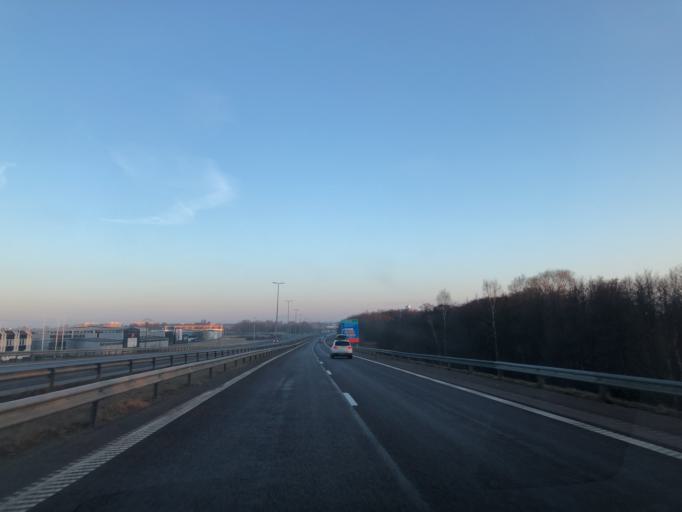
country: SE
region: Halland
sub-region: Halmstads Kommun
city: Fyllinge
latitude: 56.6458
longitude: 12.9033
